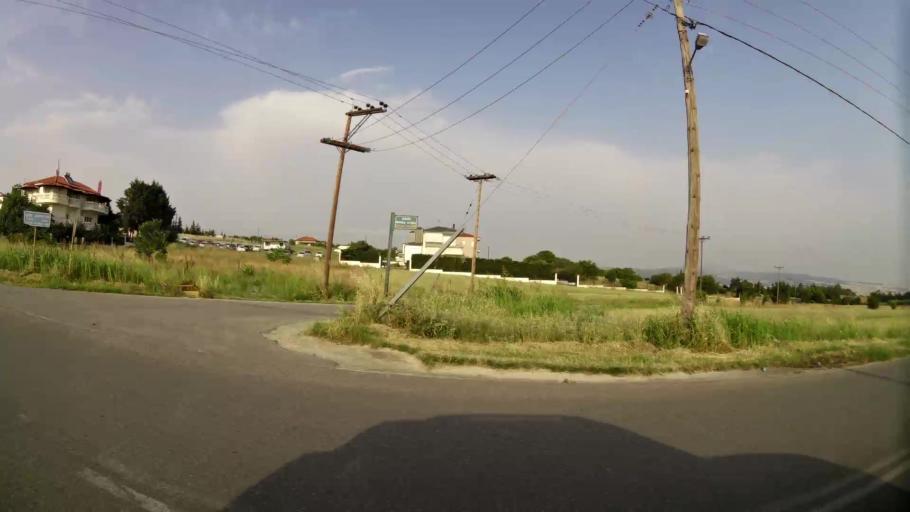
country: GR
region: Central Macedonia
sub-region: Nomos Thessalonikis
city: Oraiokastro
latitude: 40.7169
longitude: 22.9105
